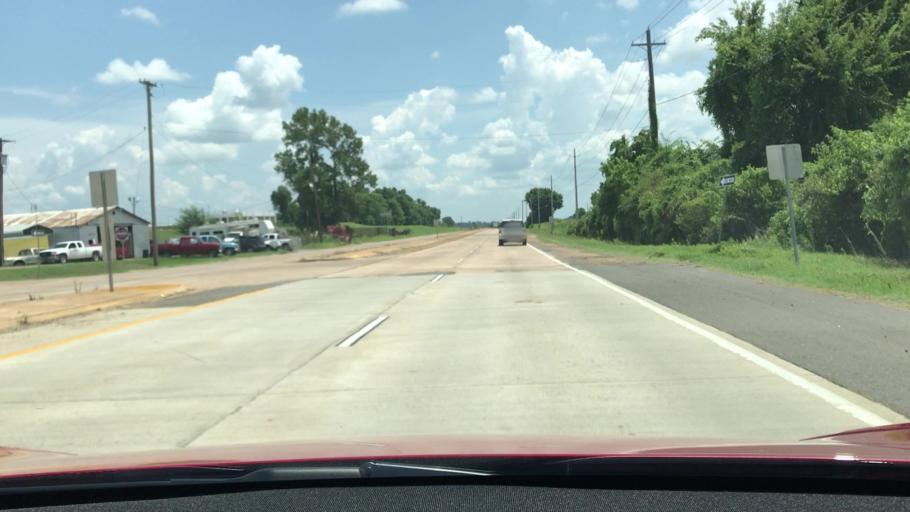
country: US
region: Louisiana
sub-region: Bossier Parish
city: Bossier City
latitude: 32.3988
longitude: -93.6916
